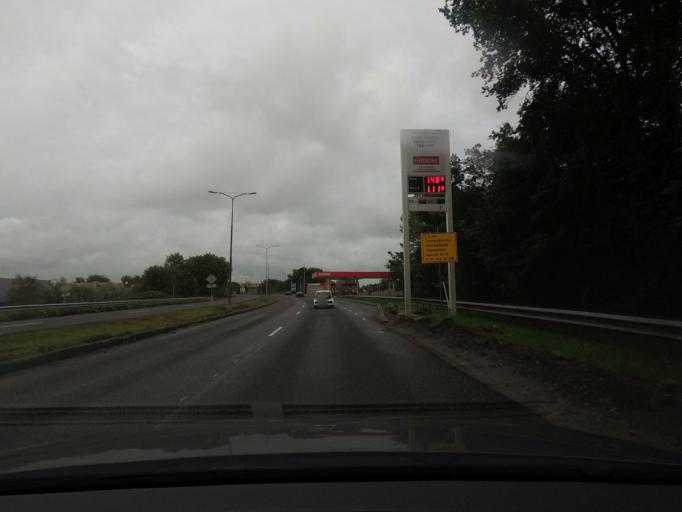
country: NL
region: North Holland
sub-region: Gemeente Alkmaar
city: Alkmaar
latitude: 52.6461
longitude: 4.7366
